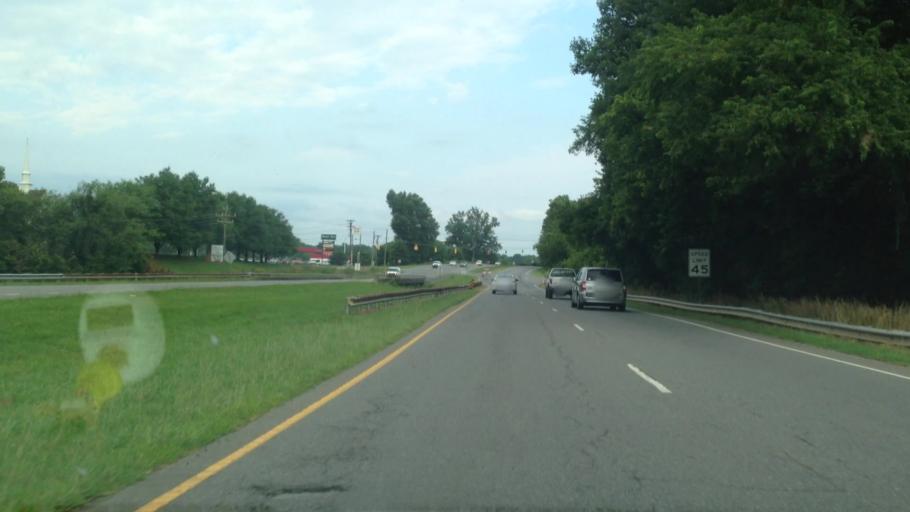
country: US
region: North Carolina
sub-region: Surry County
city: Mount Airy
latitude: 36.4799
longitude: -80.5990
